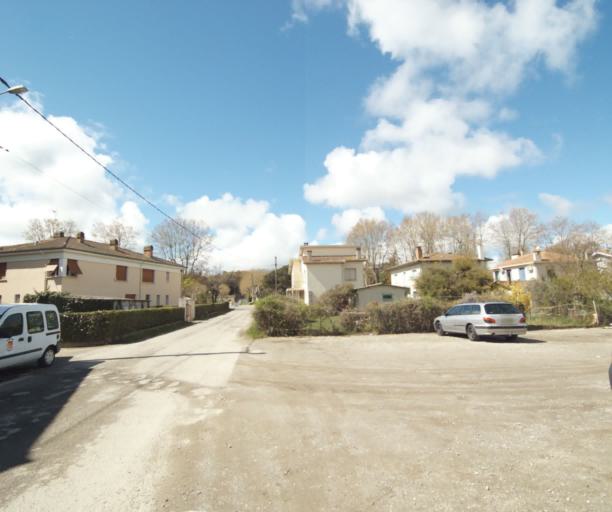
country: FR
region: Midi-Pyrenees
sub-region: Departement de l'Ariege
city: Saverdun
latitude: 43.2380
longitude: 1.5746
